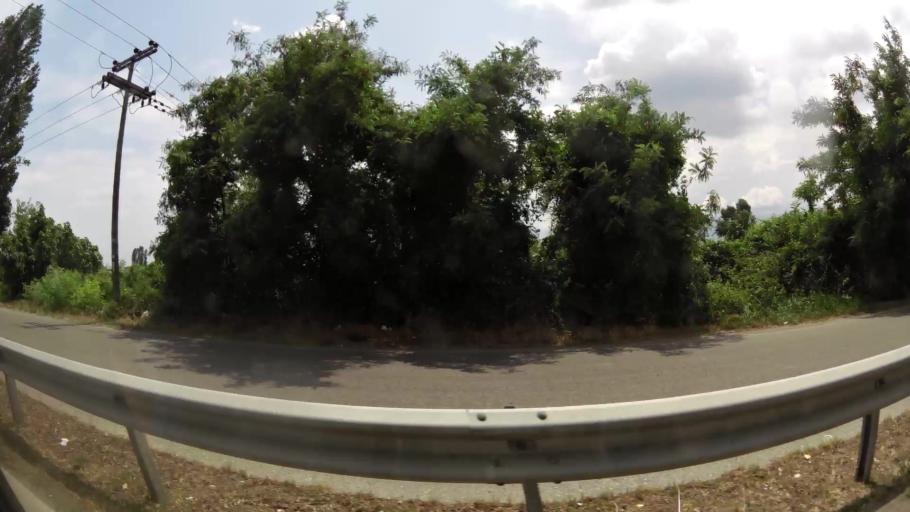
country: GR
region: Central Macedonia
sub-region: Nomos Pierias
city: Peristasi
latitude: 40.2726
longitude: 22.5550
